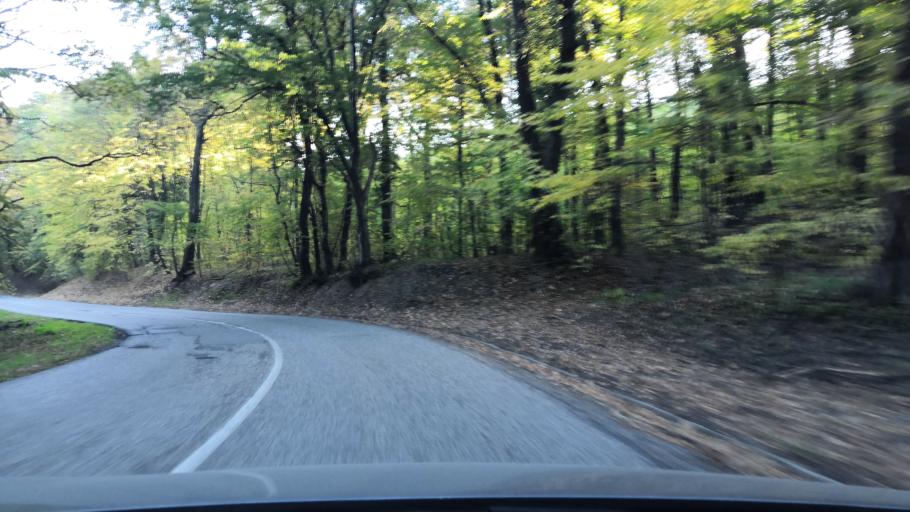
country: RS
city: Vrdnik
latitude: 45.1522
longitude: 19.7755
